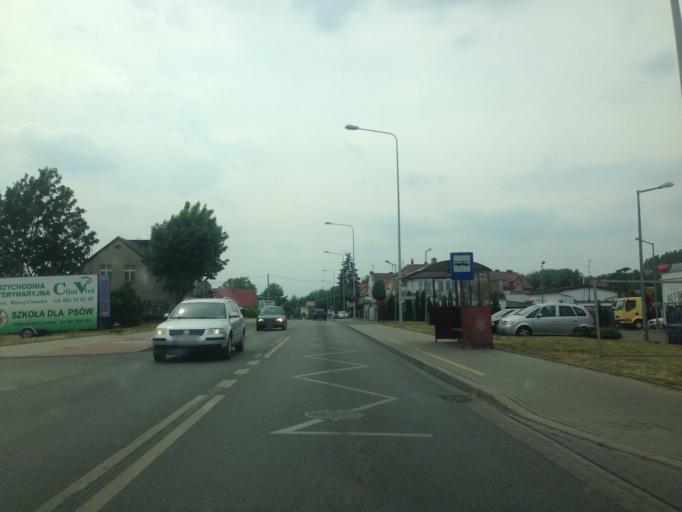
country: PL
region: Kujawsko-Pomorskie
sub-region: Grudziadz
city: Grudziadz
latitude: 53.5034
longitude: 18.7963
